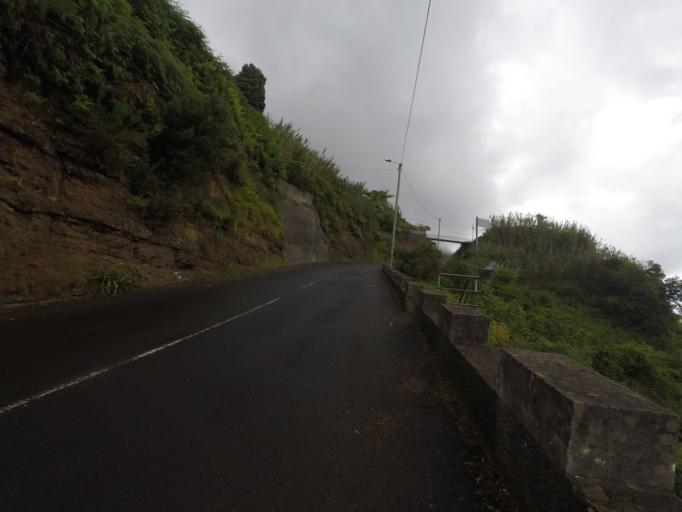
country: PT
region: Madeira
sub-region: Santana
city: Santana
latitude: 32.7690
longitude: -16.8754
